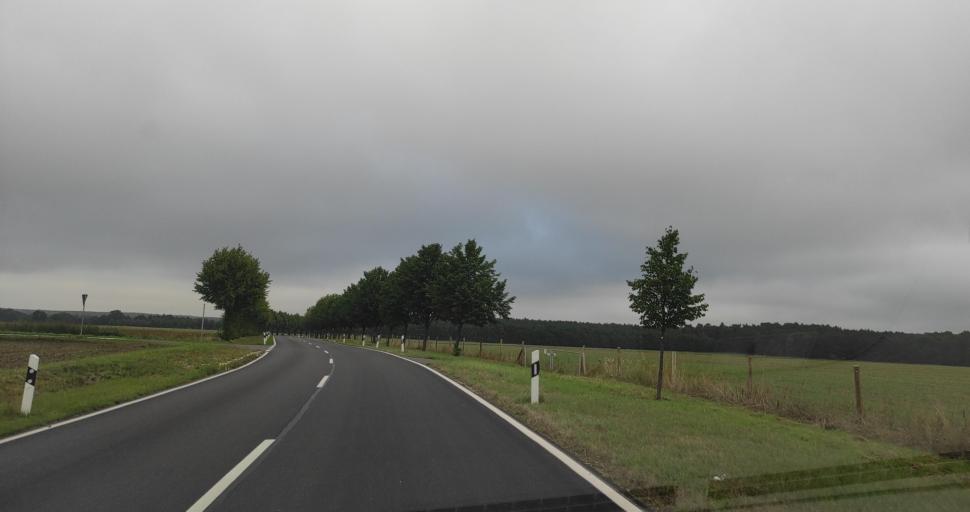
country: DE
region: Brandenburg
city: Heinersbruck
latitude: 51.7347
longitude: 14.5429
